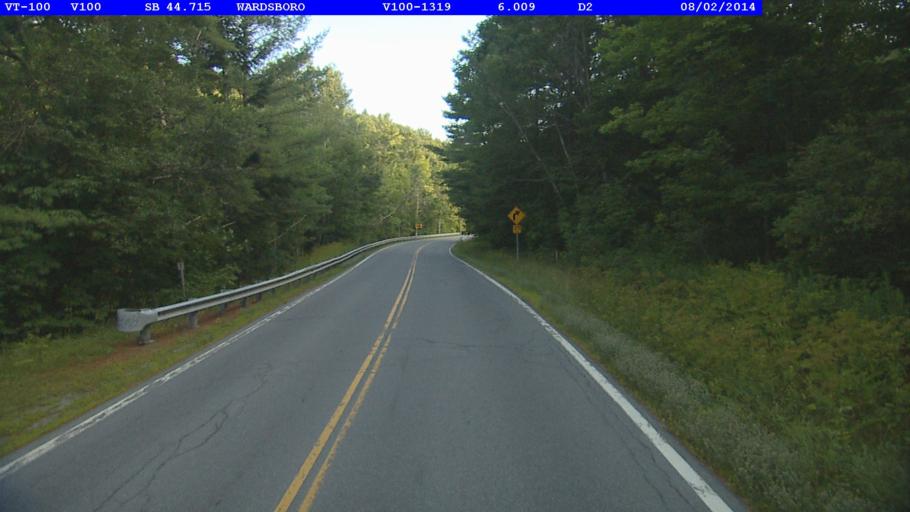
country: US
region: Vermont
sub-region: Windham County
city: Dover
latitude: 43.0353
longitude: -72.7967
